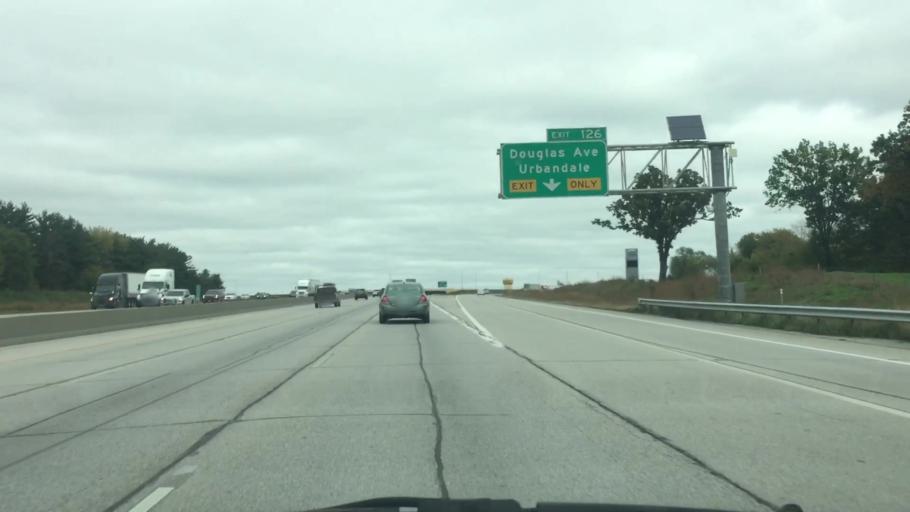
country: US
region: Iowa
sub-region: Polk County
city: Clive
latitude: 41.6233
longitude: -93.7767
